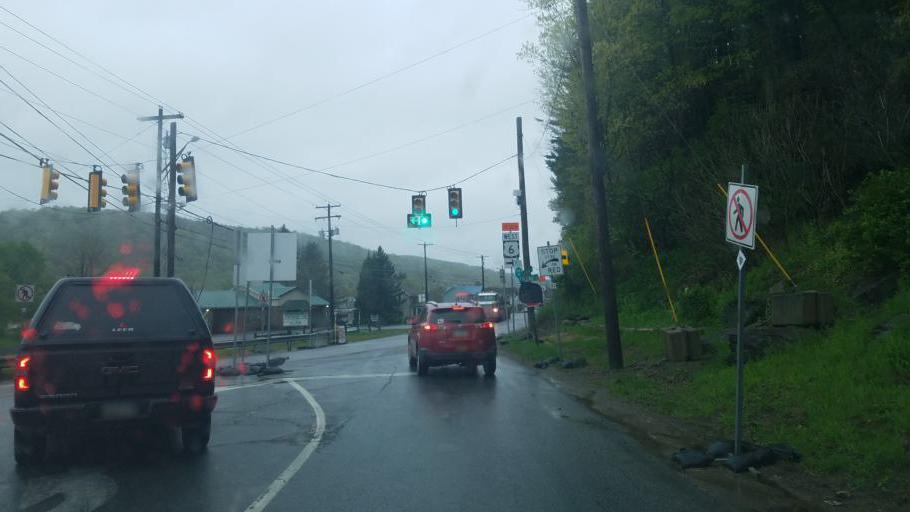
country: US
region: Pennsylvania
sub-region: Potter County
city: Coudersport
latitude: 41.7700
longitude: -78.0254
